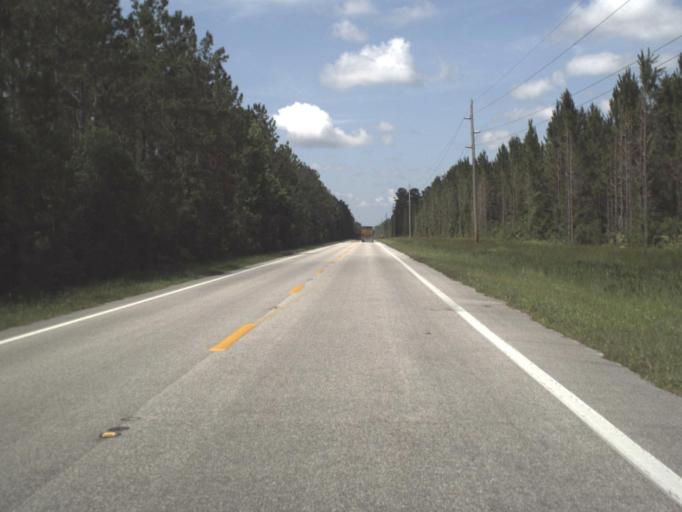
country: US
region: Florida
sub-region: Levy County
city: Bronson
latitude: 29.3725
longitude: -82.7186
